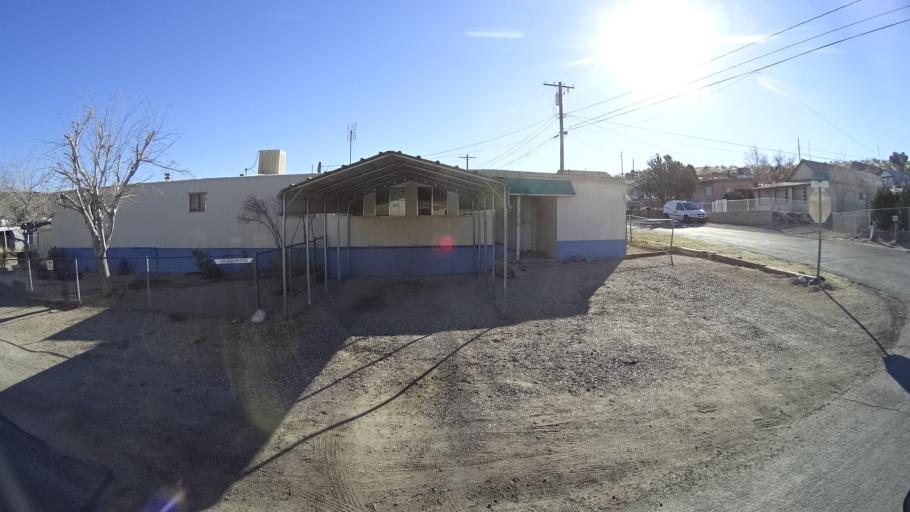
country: US
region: Arizona
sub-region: Mohave County
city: Kingman
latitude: 35.1845
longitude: -114.0536
